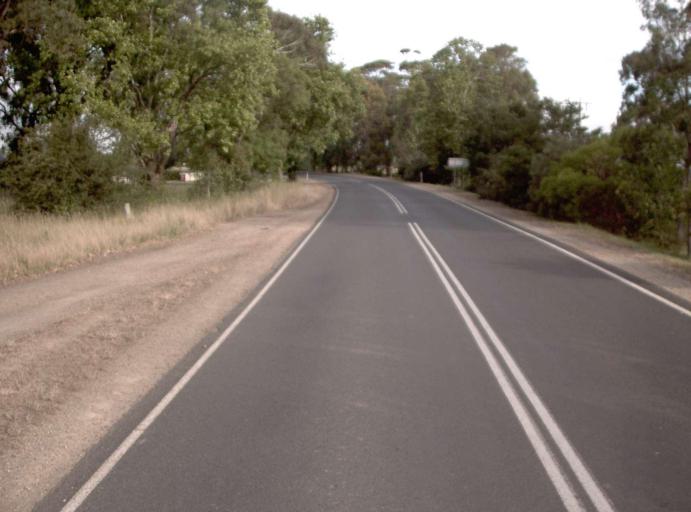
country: AU
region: Victoria
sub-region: Wellington
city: Heyfield
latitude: -37.9640
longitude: 146.8995
